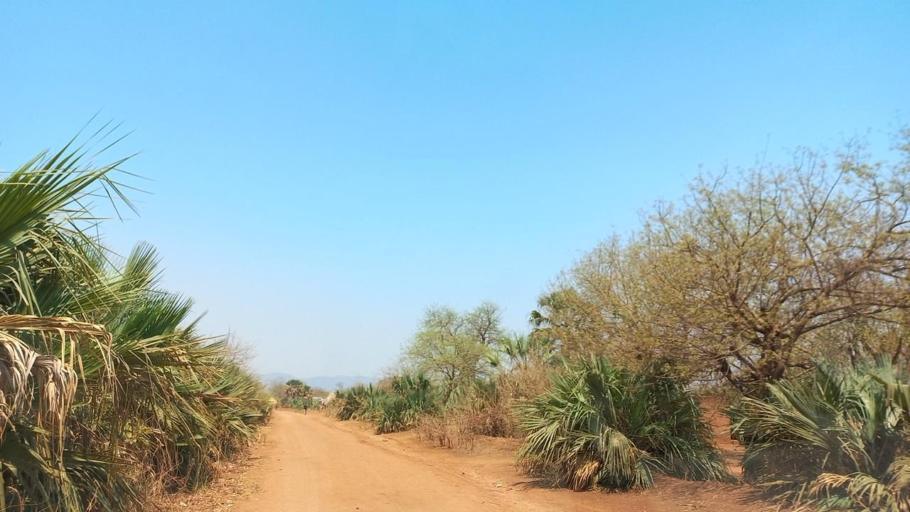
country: ZM
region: Lusaka
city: Luangwa
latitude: -15.1871
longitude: 30.2087
